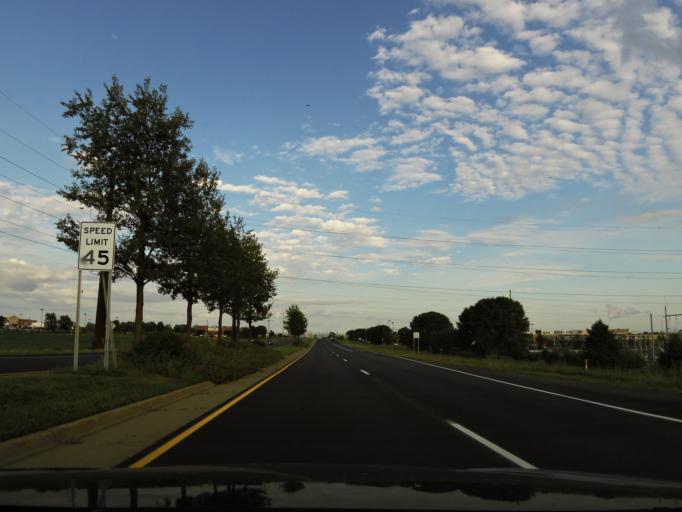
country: US
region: Minnesota
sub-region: Dakota County
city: Hastings
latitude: 44.7384
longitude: -92.8965
